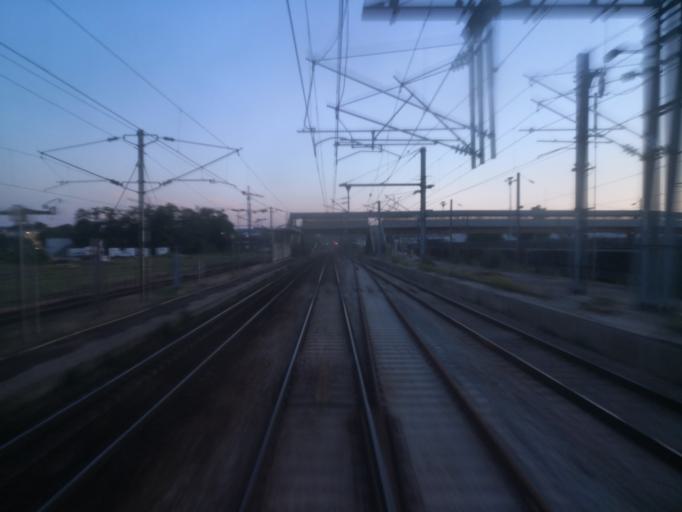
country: FR
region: Ile-de-France
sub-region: Departement des Yvelines
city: Poissy
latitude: 48.9385
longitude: 2.0529
